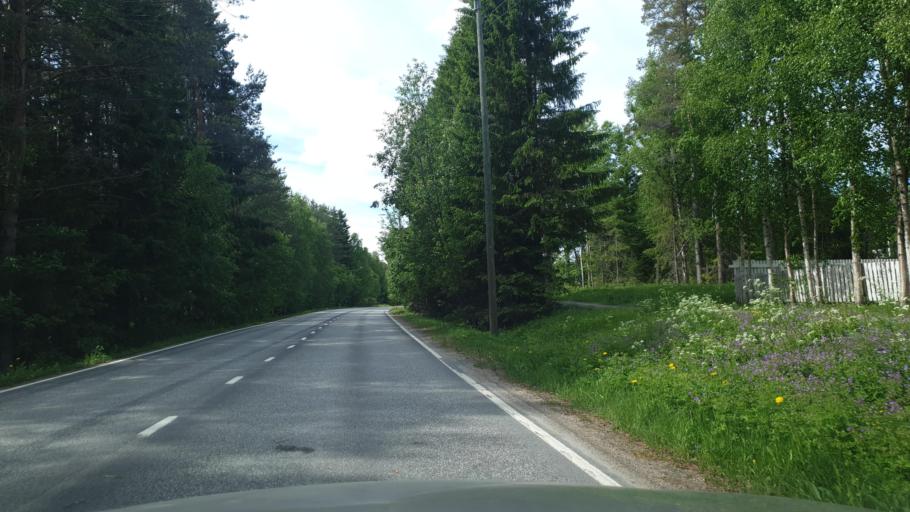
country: FI
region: Northern Ostrobothnia
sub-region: Oulunkaari
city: Ii
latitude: 65.3160
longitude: 25.3965
